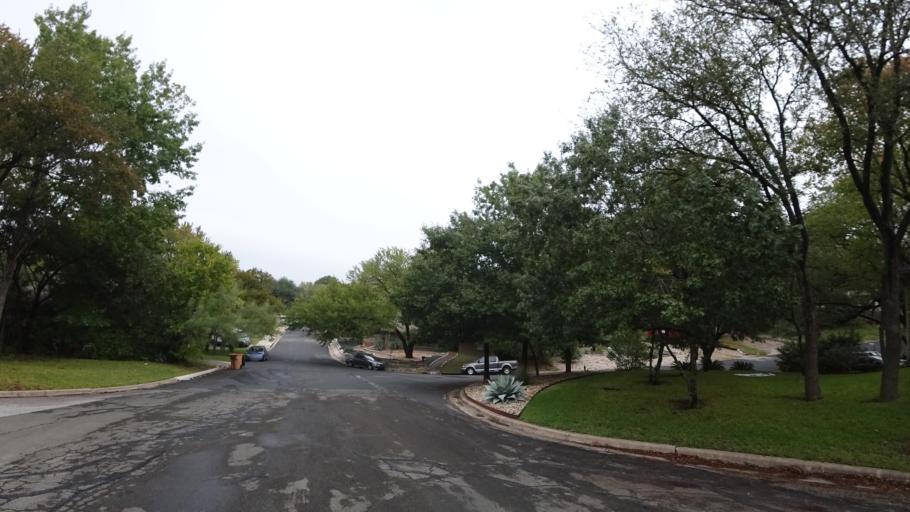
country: US
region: Texas
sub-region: Travis County
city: Rollingwood
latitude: 30.2526
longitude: -97.7805
